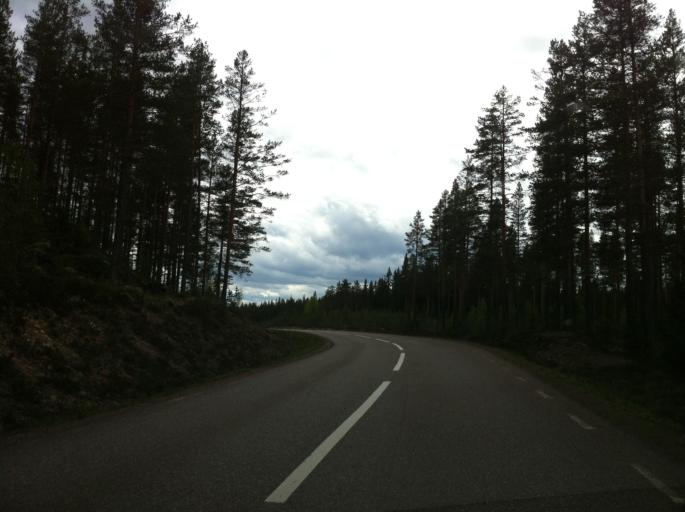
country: NO
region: Hedmark
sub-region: Trysil
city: Innbygda
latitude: 61.3610
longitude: 13.0578
